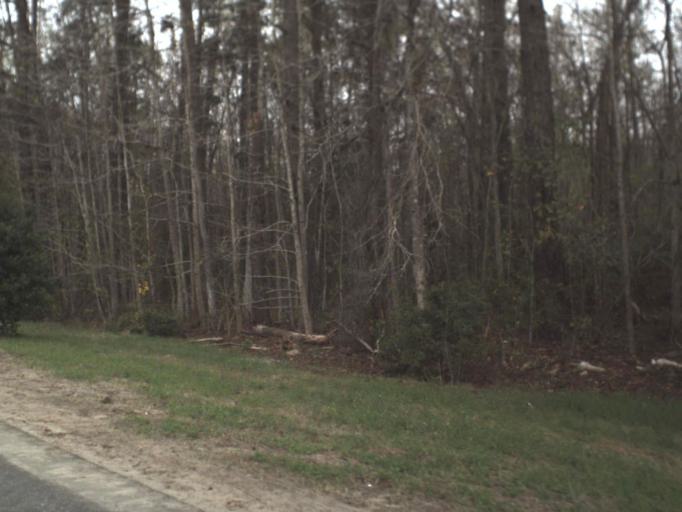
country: US
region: Florida
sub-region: Jefferson County
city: Monticello
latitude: 30.4937
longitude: -83.7359
